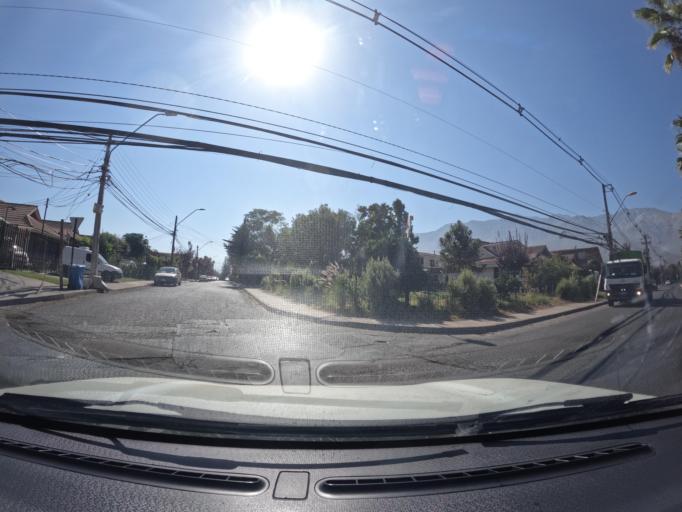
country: CL
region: Santiago Metropolitan
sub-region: Provincia de Santiago
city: Villa Presidente Frei, Nunoa, Santiago, Chile
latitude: -33.4808
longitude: -70.5523
